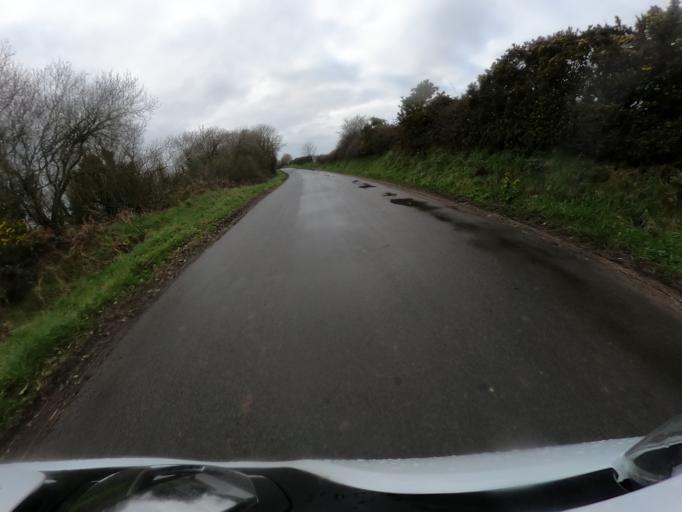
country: IM
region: Ramsey
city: Ramsey
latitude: 54.3640
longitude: -4.4803
